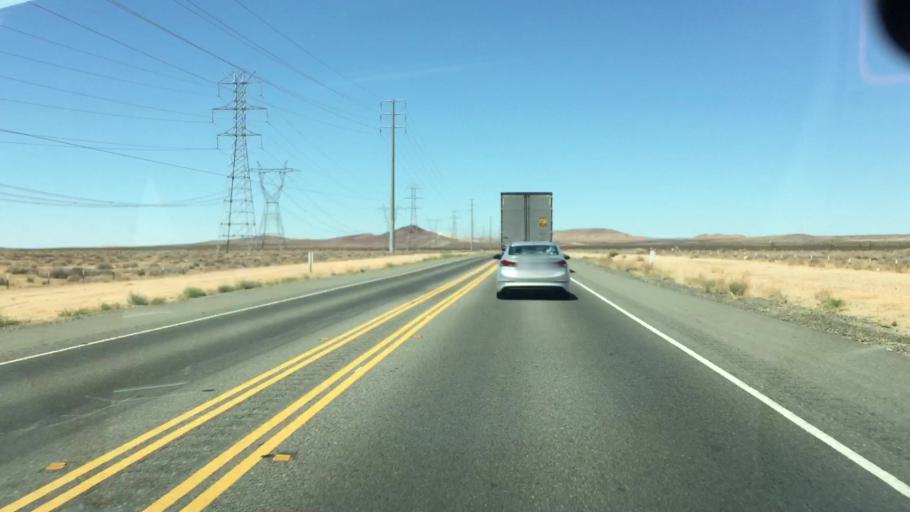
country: US
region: California
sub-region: Kern County
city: Boron
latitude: 34.8335
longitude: -117.4976
